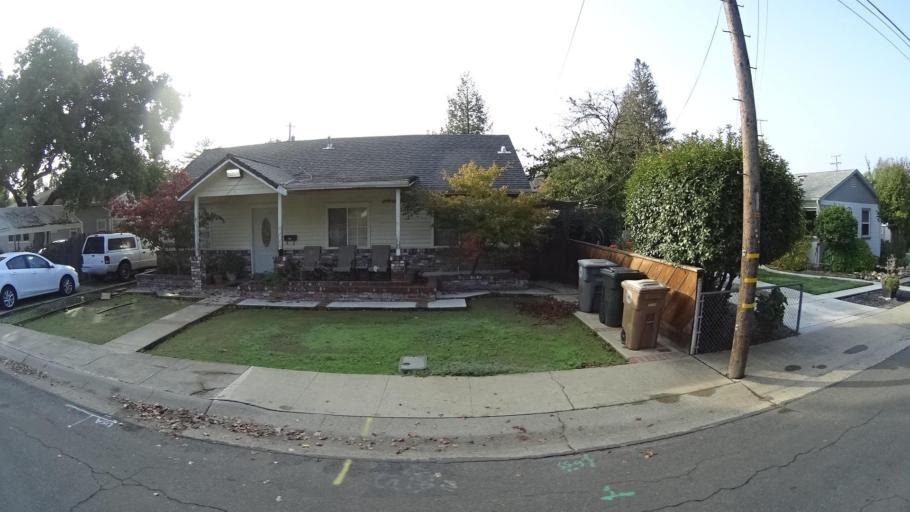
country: US
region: California
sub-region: Sacramento County
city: Elk Grove
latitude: 38.4075
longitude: -121.3696
